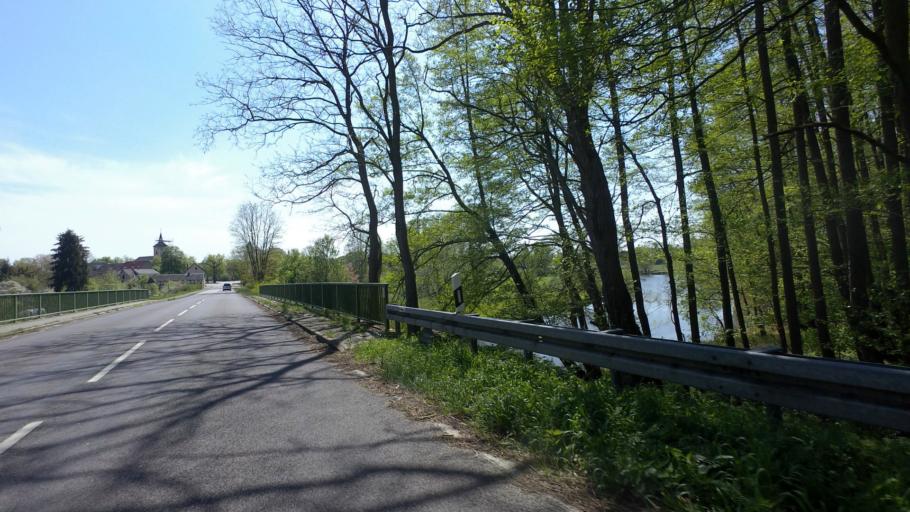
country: DE
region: Brandenburg
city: Halbe
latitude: 52.1109
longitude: 13.7585
